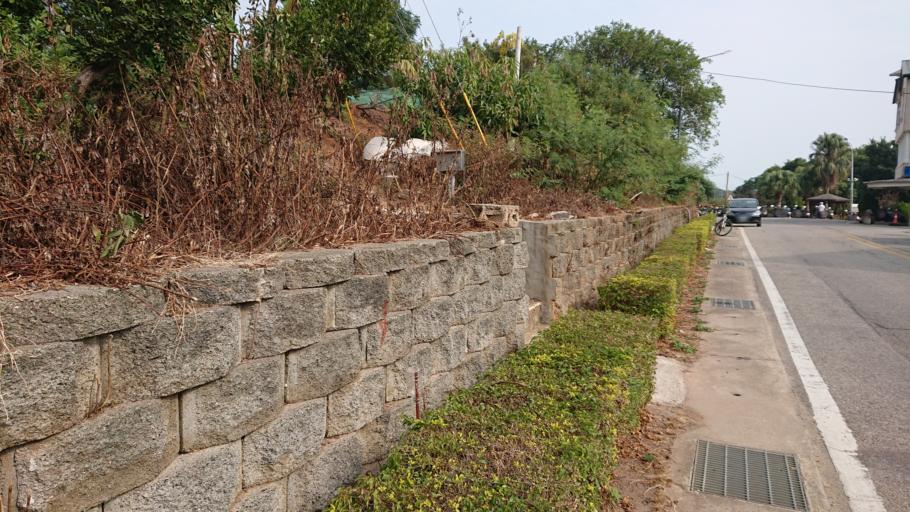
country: TW
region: Fukien
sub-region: Kinmen
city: Jincheng
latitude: 24.4296
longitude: 118.2493
